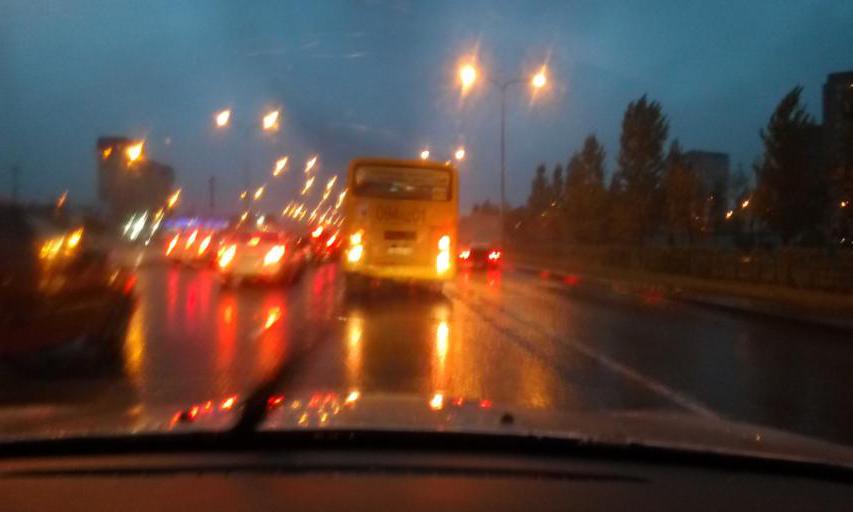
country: KZ
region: Astana Qalasy
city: Astana
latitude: 51.1820
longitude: 71.3715
